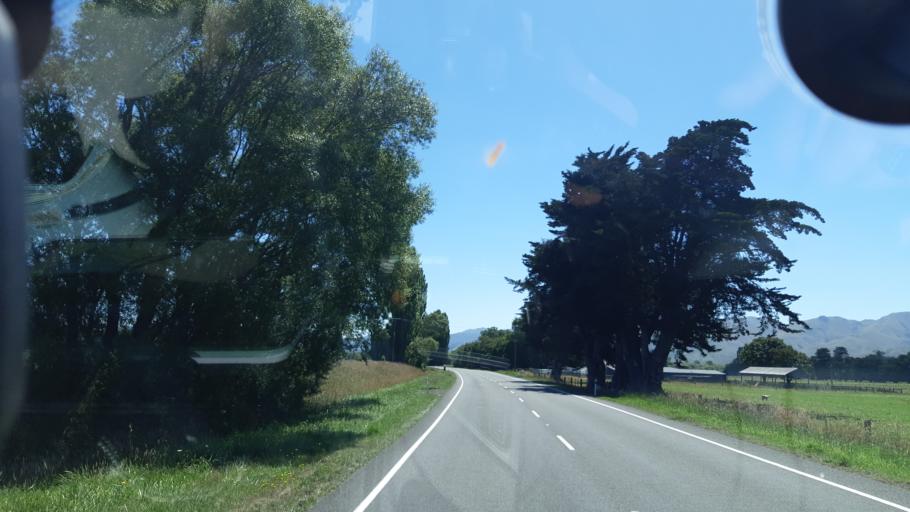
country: NZ
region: Canterbury
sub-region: Kaikoura District
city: Kaikoura
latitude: -42.7356
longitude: 173.2712
